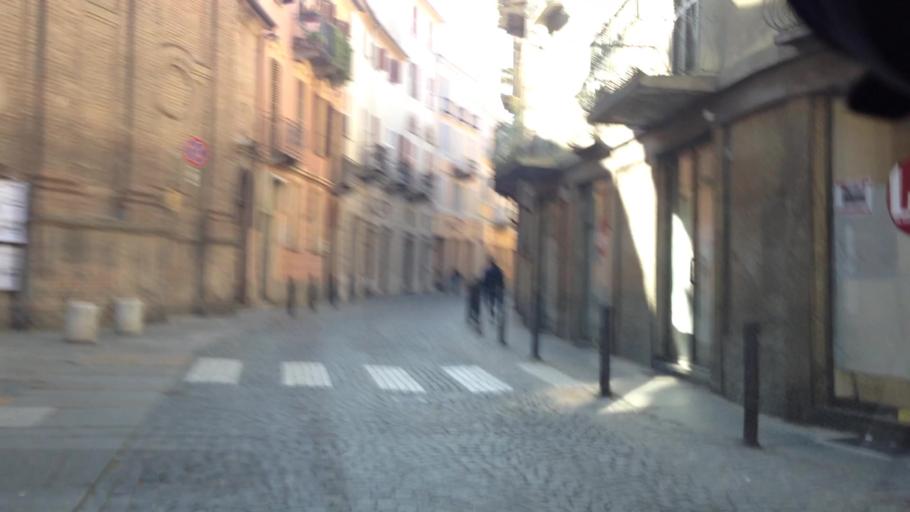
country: IT
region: Piedmont
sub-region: Provincia di Asti
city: Asti
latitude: 44.8979
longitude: 8.2044
